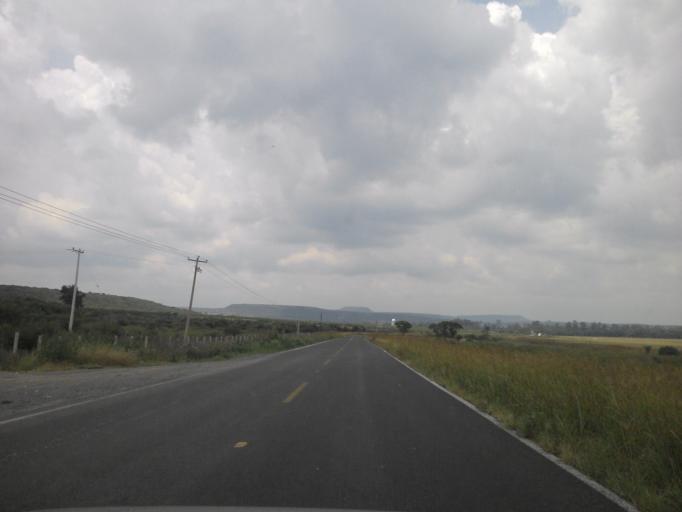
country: MX
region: Jalisco
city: San Diego de Alejandria
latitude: 20.8626
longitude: -101.9949
